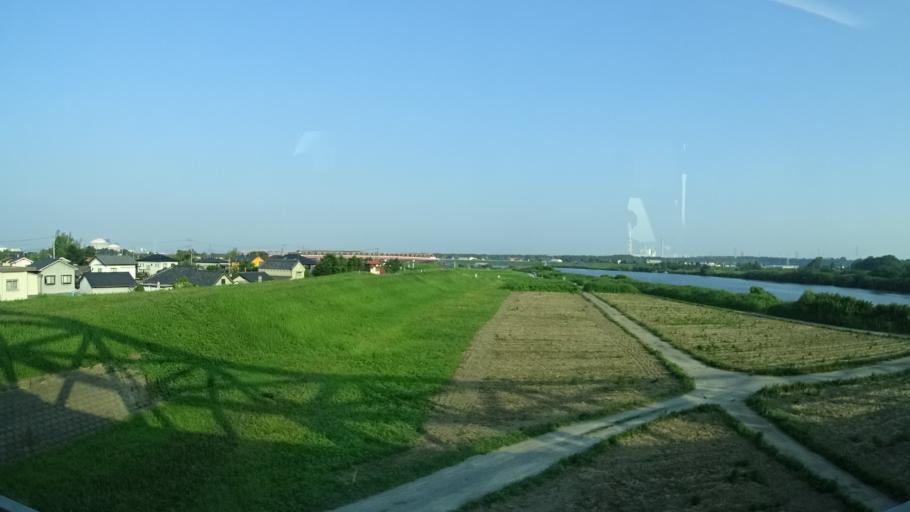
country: JP
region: Ibaraki
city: Funaishikawa
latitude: 36.4876
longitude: 140.5988
